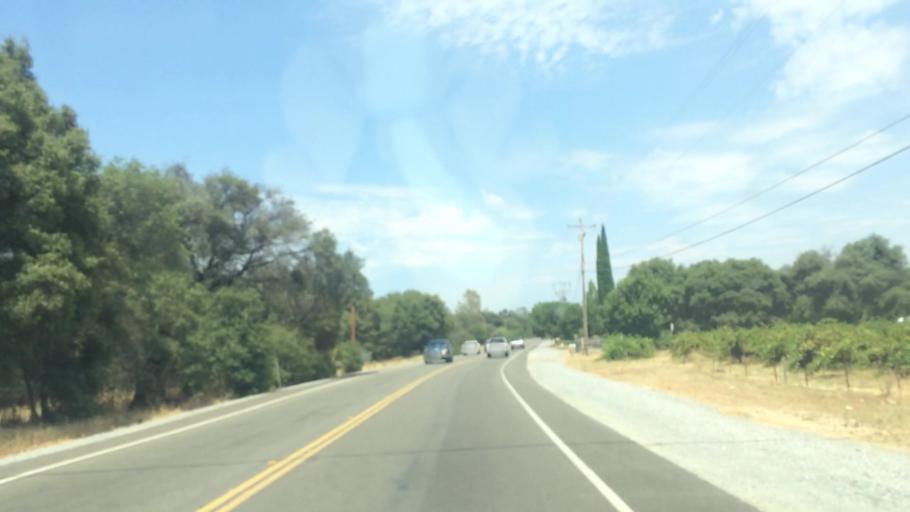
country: US
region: California
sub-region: Amador County
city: Sutter Creek
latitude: 38.3901
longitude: -120.7707
